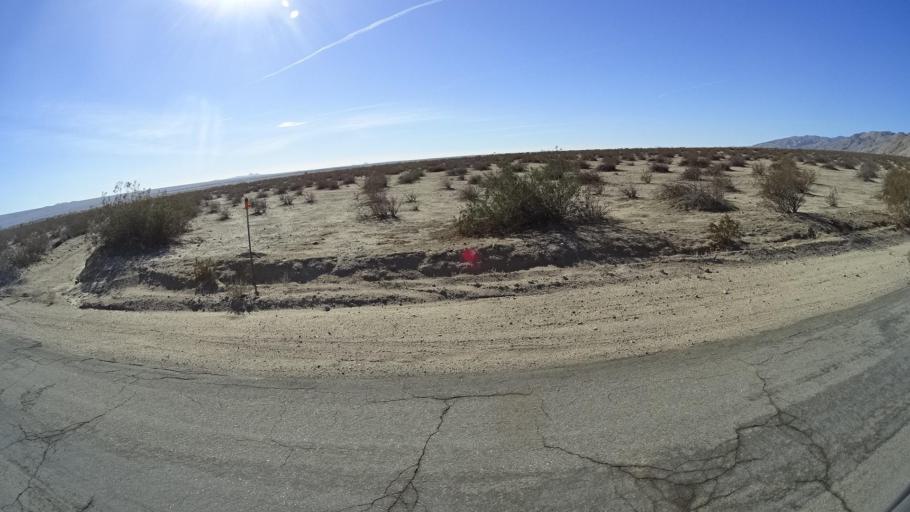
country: US
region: California
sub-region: Kern County
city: California City
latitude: 35.3012
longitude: -117.9929
